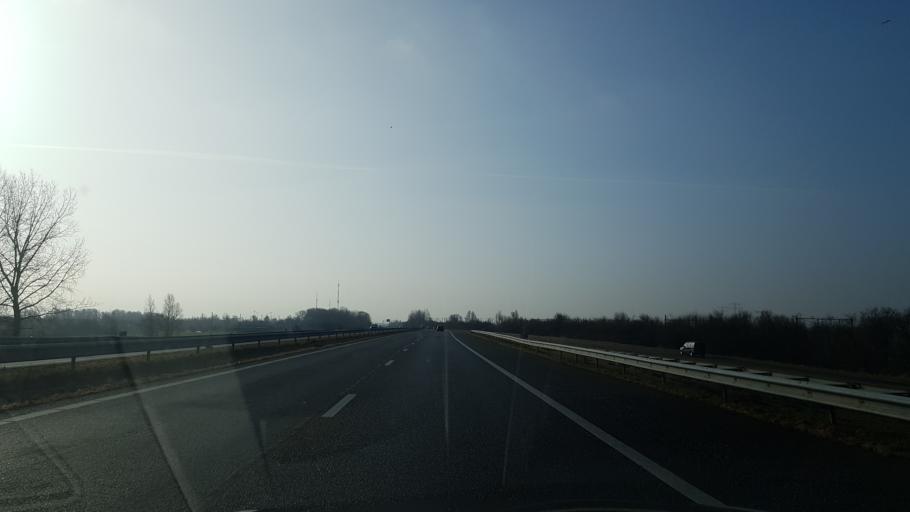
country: NL
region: Friesland
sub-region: Gemeente Boarnsterhim
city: Grou
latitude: 53.0904
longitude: 5.8234
